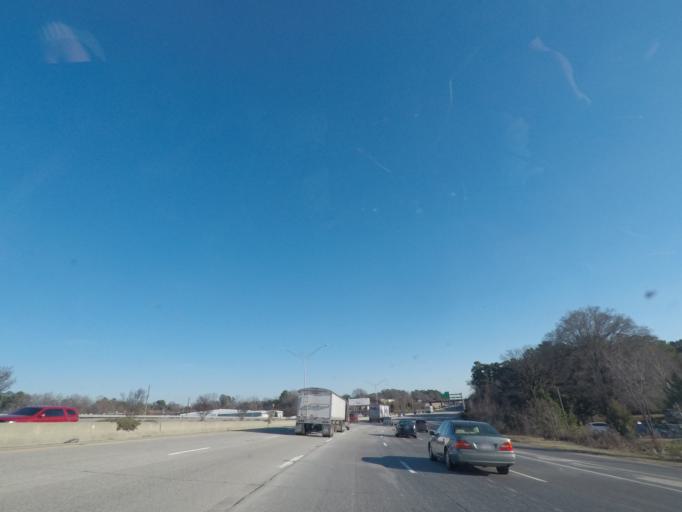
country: US
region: North Carolina
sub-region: Durham County
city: Durham
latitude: 36.0281
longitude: -78.9212
